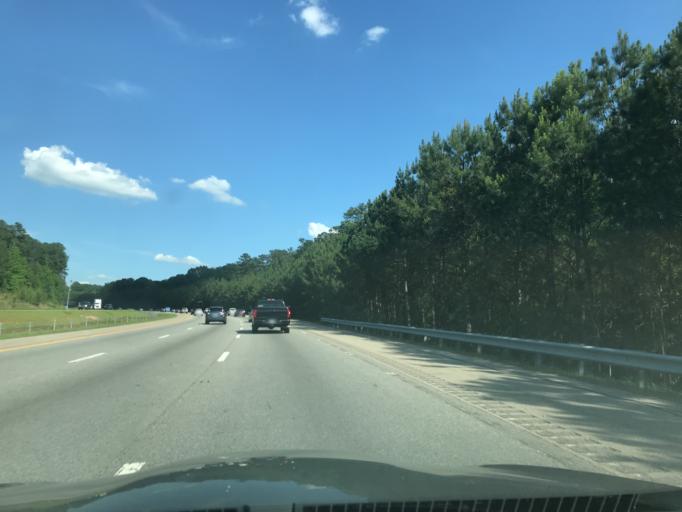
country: US
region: North Carolina
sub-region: Wake County
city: West Raleigh
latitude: 35.9008
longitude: -78.6300
